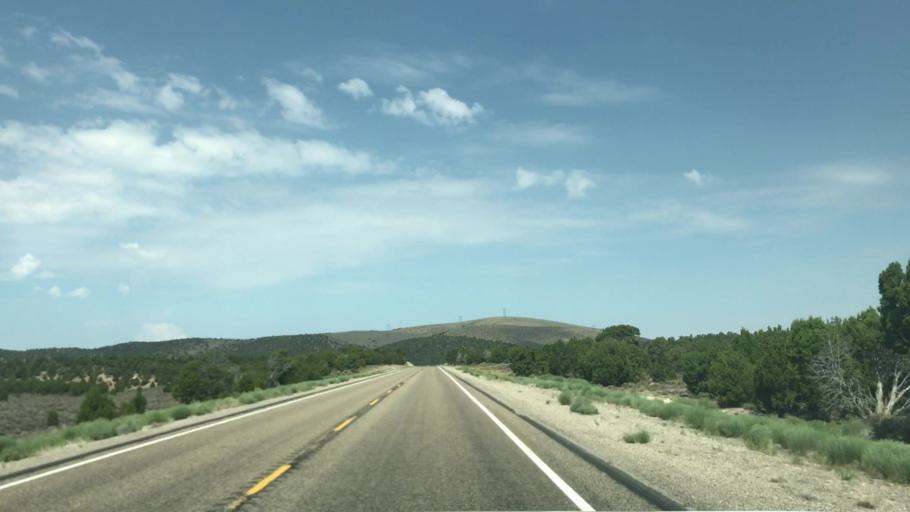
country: US
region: Nevada
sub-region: White Pine County
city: Ely
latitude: 39.3864
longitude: -115.0737
